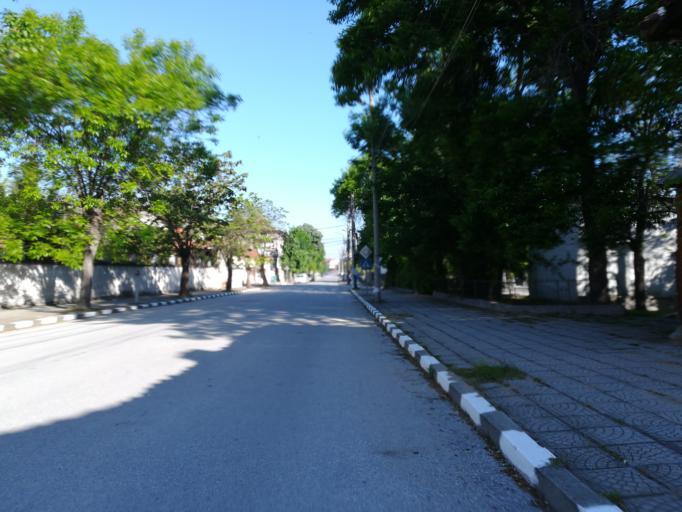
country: BG
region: Stara Zagora
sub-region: Obshtina Chirpan
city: Chirpan
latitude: 42.1019
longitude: 25.2237
